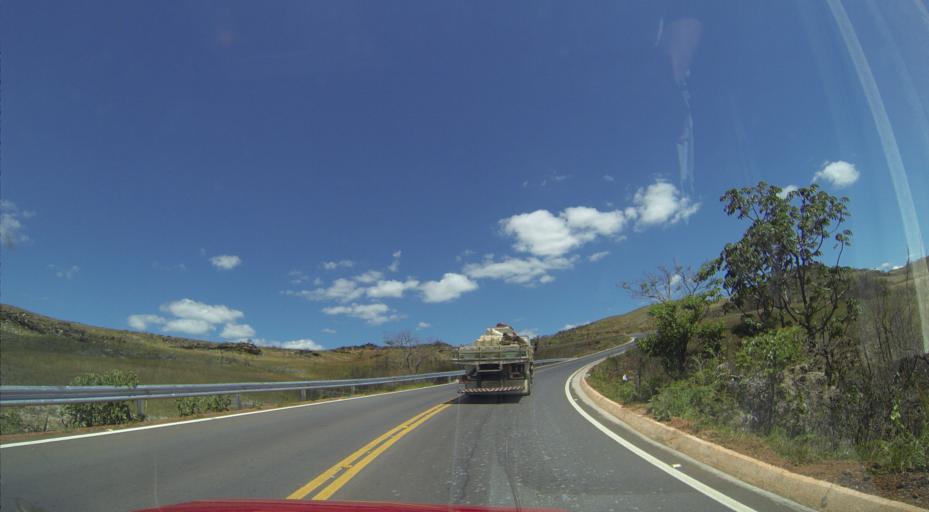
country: BR
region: Minas Gerais
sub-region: Conceicao Do Mato Dentro
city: Conceicao do Mato Dentro
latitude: -19.2845
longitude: -43.5769
